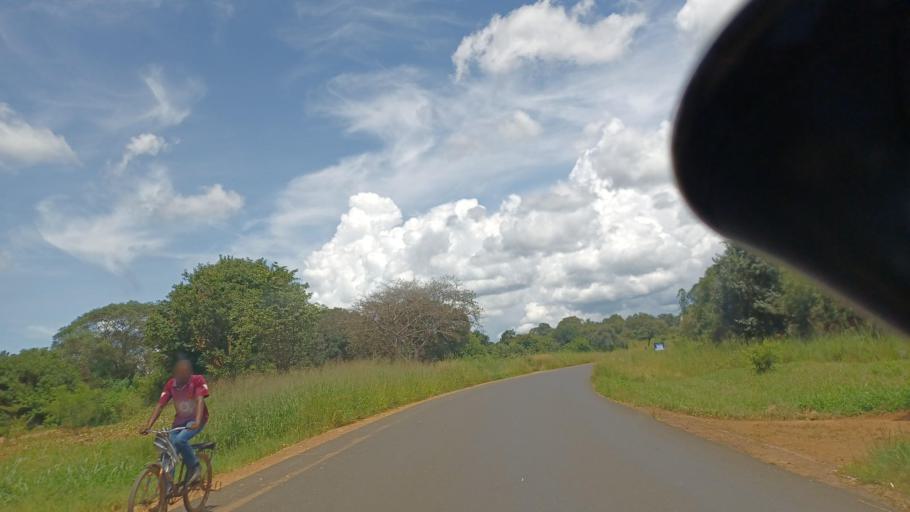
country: ZM
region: North-Western
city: Solwezi
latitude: -12.4046
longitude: 26.2402
